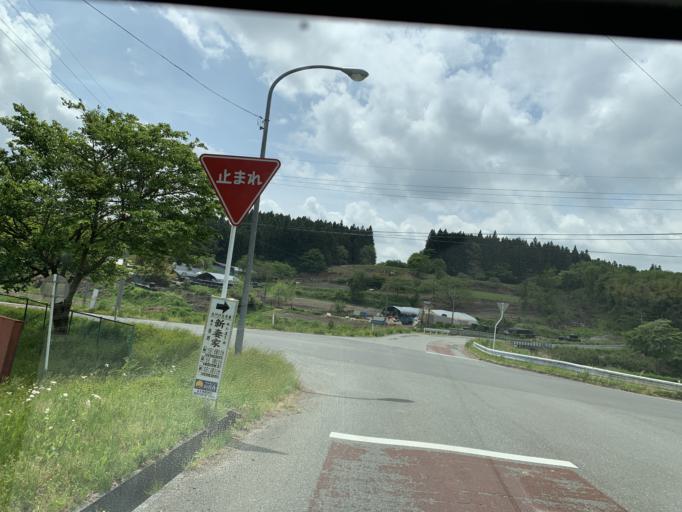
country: JP
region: Miyagi
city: Furukawa
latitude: 38.7318
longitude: 140.9277
